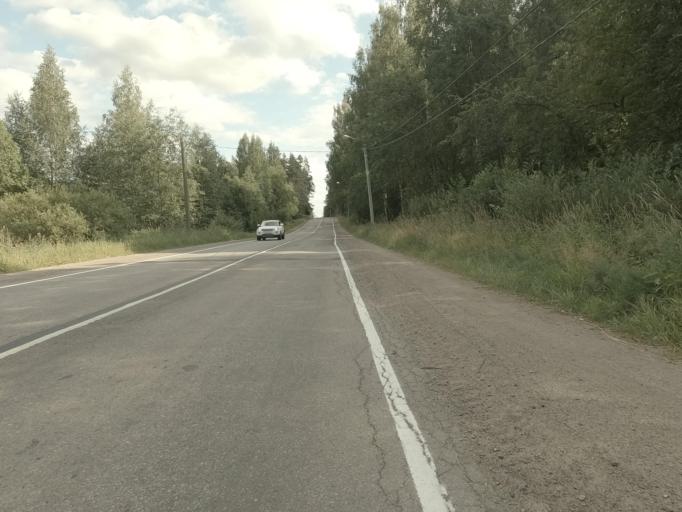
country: RU
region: Leningrad
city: Kamennogorsk
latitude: 60.9384
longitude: 29.1563
